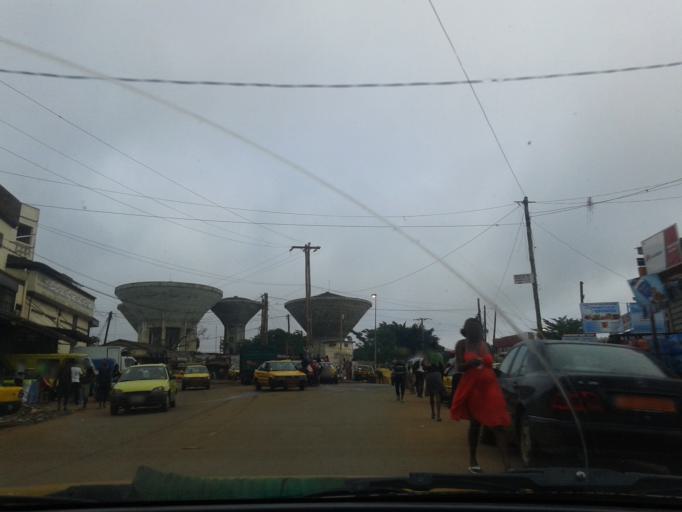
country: CM
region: Centre
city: Yaounde
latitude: 3.8825
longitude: 11.5242
